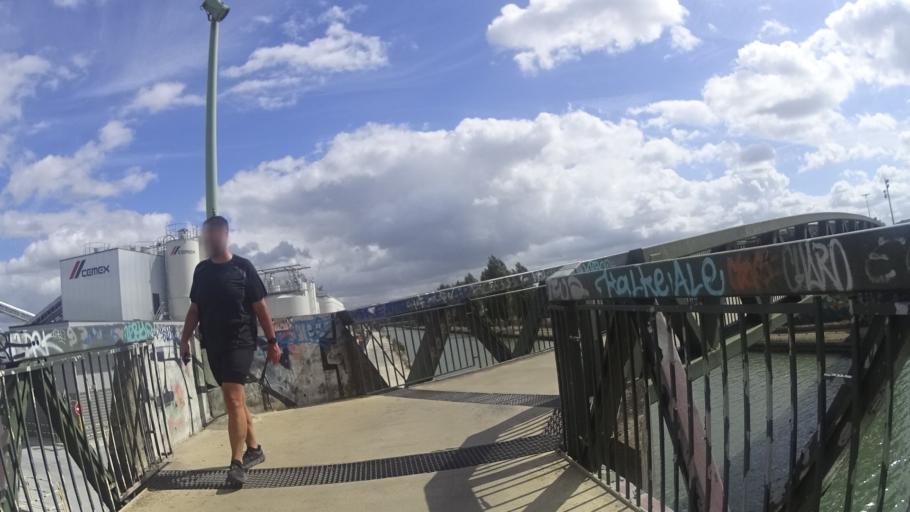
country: FR
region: Ile-de-France
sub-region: Departement de Seine-Saint-Denis
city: Bondy
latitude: 48.9060
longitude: 2.4736
